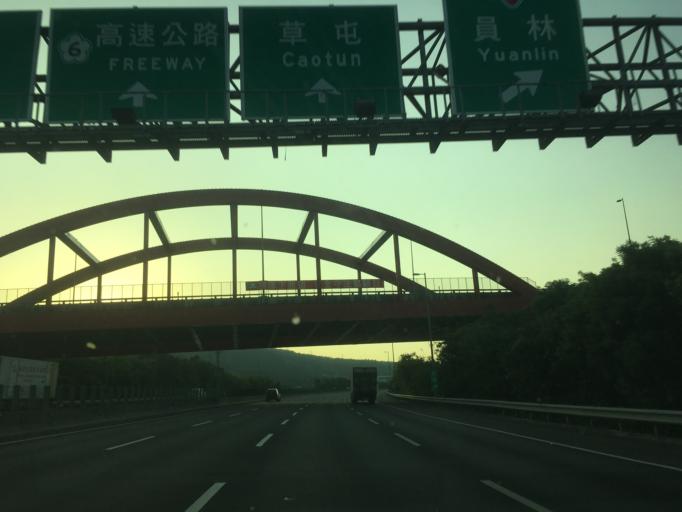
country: TW
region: Taiwan
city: Zhongxing New Village
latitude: 23.9581
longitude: 120.6557
